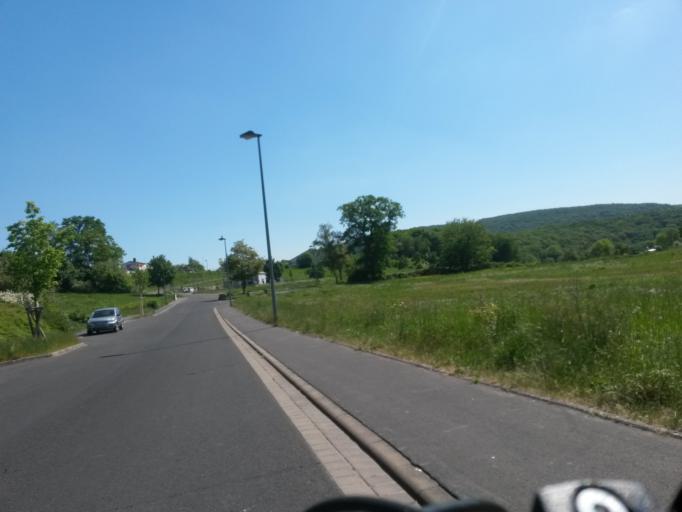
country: DE
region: Bavaria
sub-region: Regierungsbezirk Unterfranken
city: Bad Kissingen
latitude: 50.1823
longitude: 10.0772
